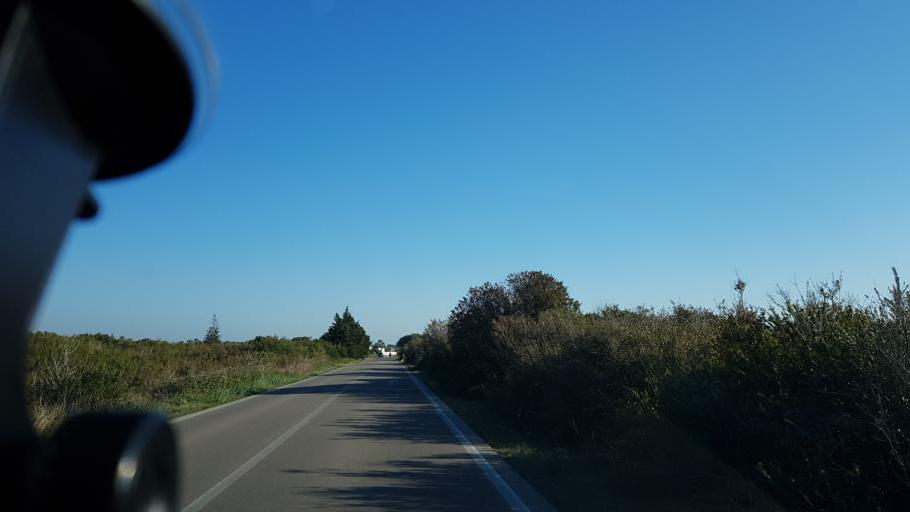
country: IT
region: Apulia
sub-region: Provincia di Lecce
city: Merine
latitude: 40.4346
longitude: 18.2401
